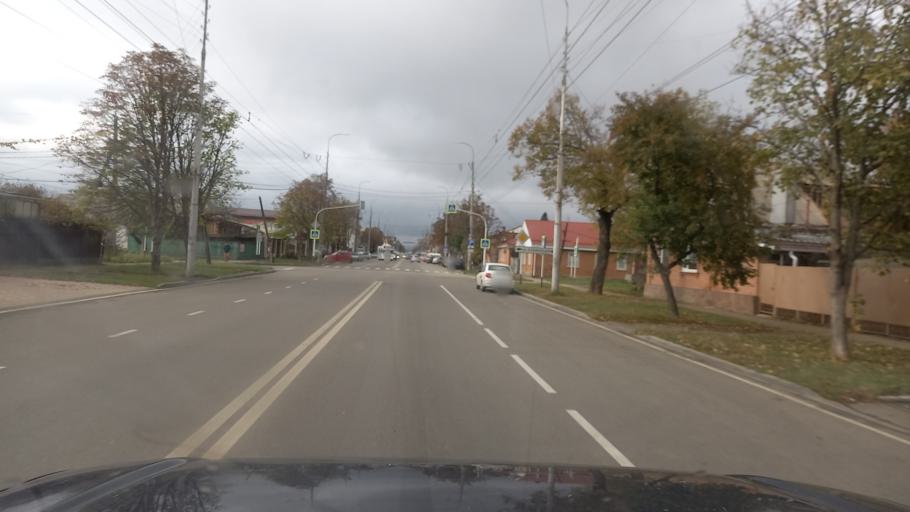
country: RU
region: Adygeya
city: Maykop
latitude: 44.6082
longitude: 40.1150
